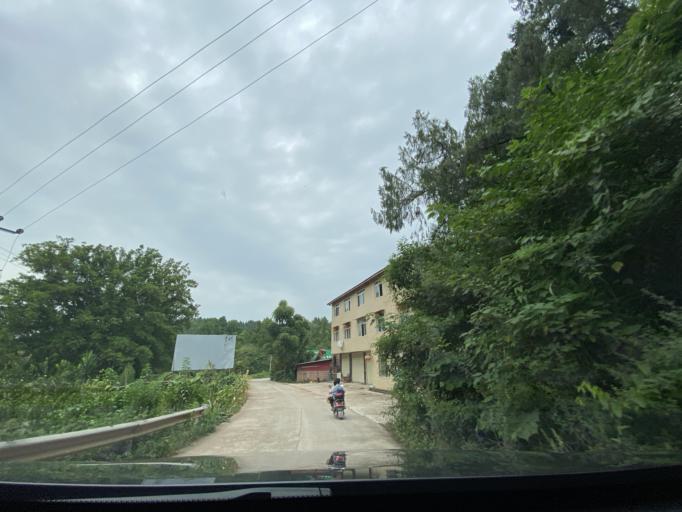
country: CN
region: Sichuan
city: Jiancheng
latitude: 30.3880
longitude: 104.5149
